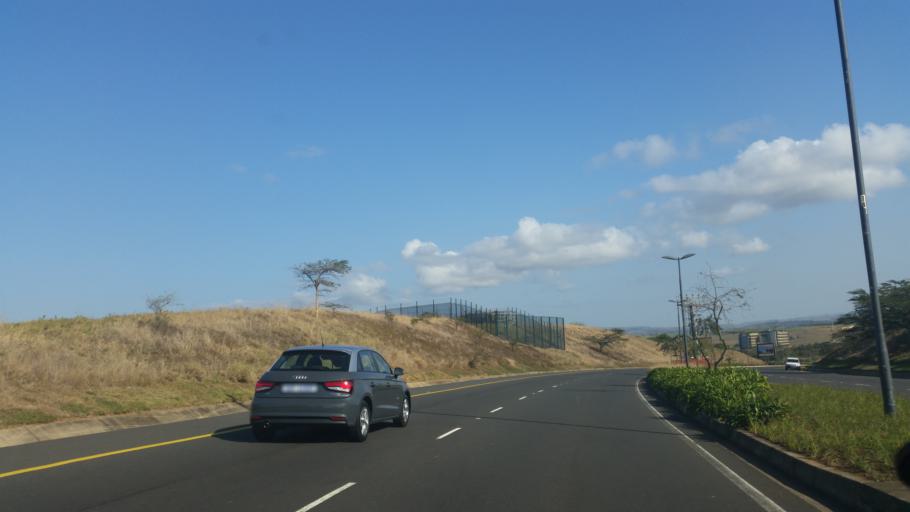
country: ZA
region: KwaZulu-Natal
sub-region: iLembe District Municipality
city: Ballitoville
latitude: -29.6283
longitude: 31.1061
